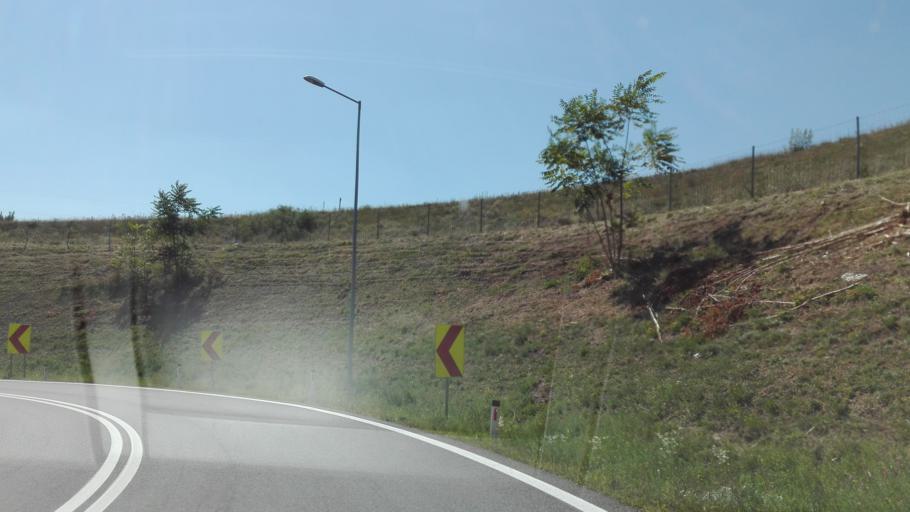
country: AT
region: Lower Austria
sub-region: Politischer Bezirk Wien-Umgebung
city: Lanzendorf
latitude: 48.1243
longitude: 16.4354
